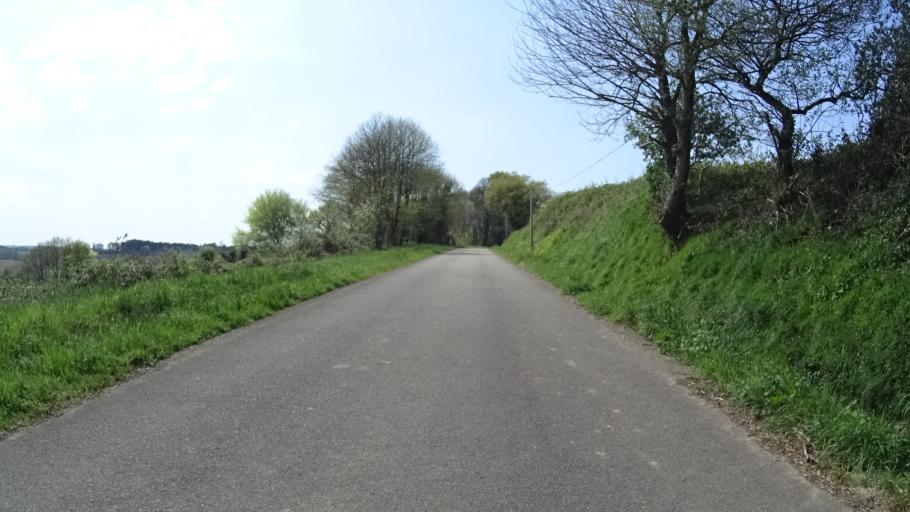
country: FR
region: Brittany
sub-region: Departement du Finistere
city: Sizun
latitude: 48.4400
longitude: -4.1045
